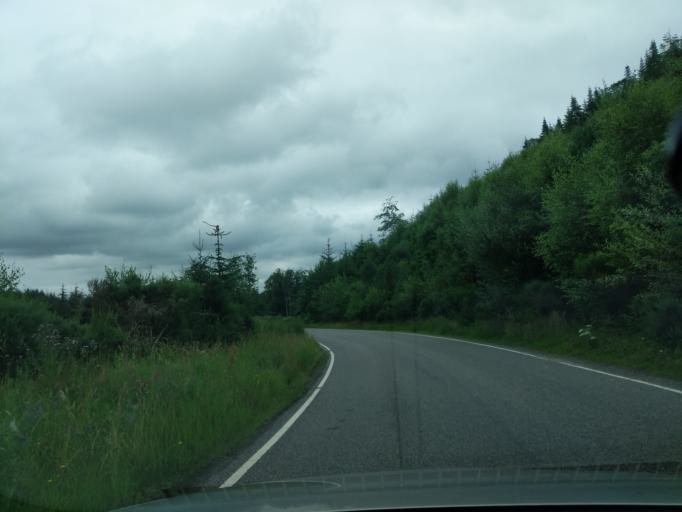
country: GB
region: Scotland
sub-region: Moray
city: Forres
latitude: 57.5199
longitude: -3.6783
